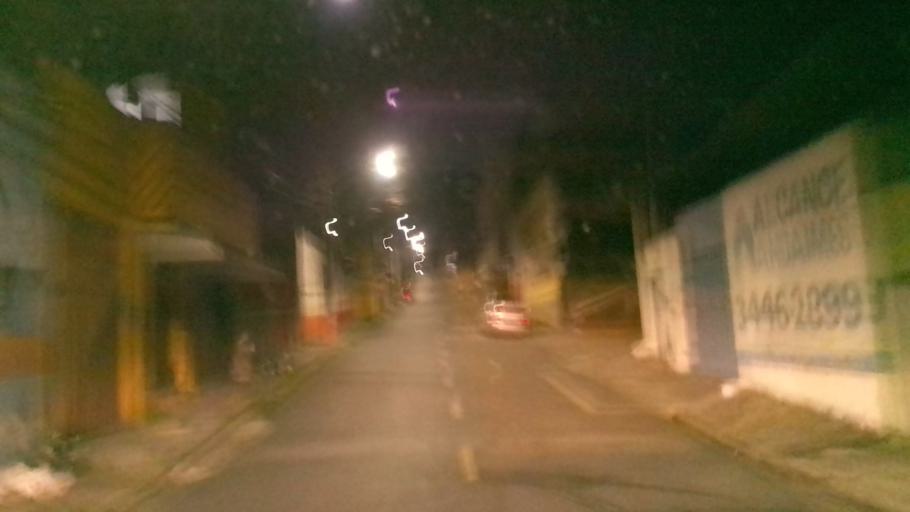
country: BR
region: Minas Gerais
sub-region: Belo Horizonte
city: Belo Horizonte
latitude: -19.9043
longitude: -43.9547
